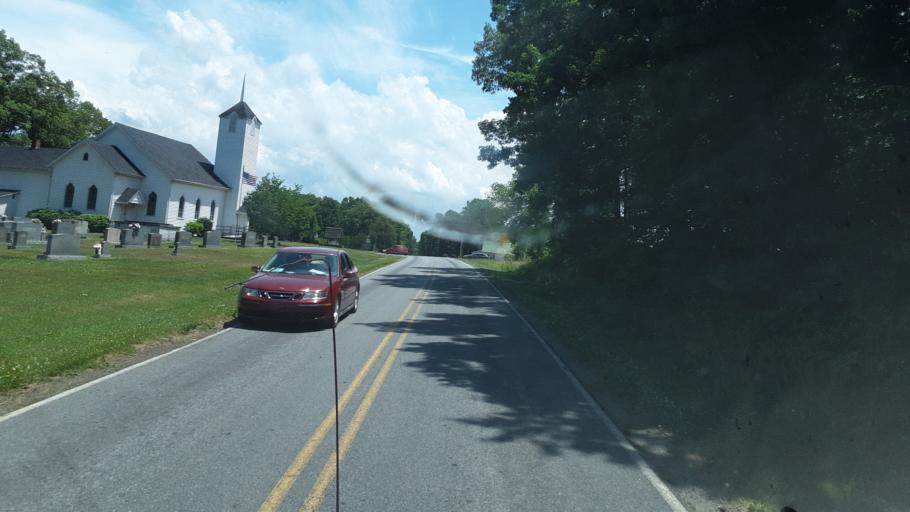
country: US
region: North Carolina
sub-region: Yadkin County
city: Jonesville
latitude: 36.0863
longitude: -80.8626
